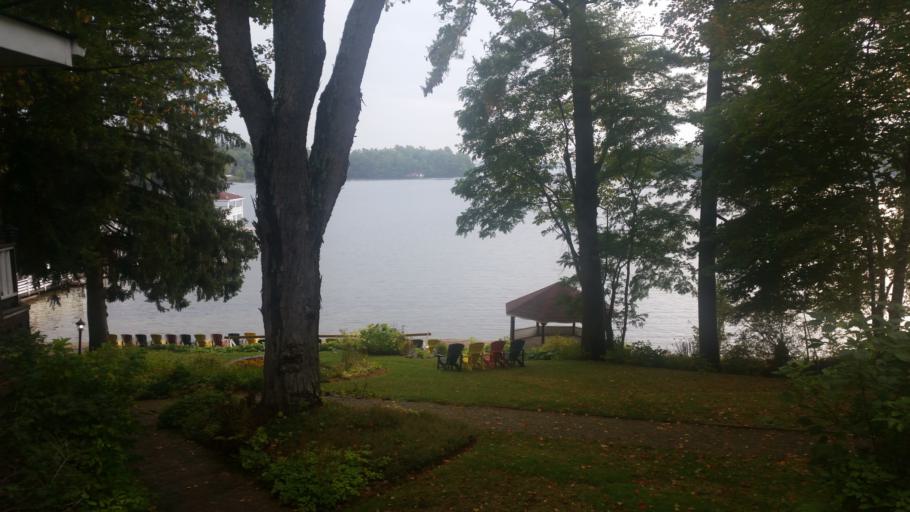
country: CA
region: Ontario
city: Bracebridge
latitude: 45.1648
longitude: -79.6475
